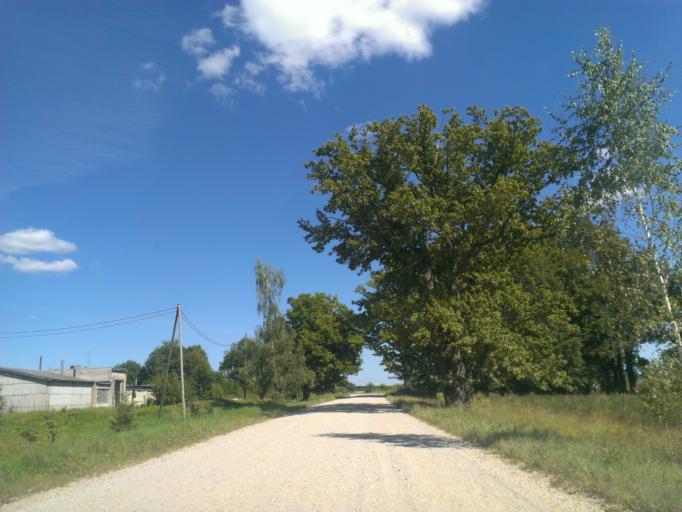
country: LV
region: Malpils
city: Malpils
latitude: 57.0067
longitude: 24.9843
